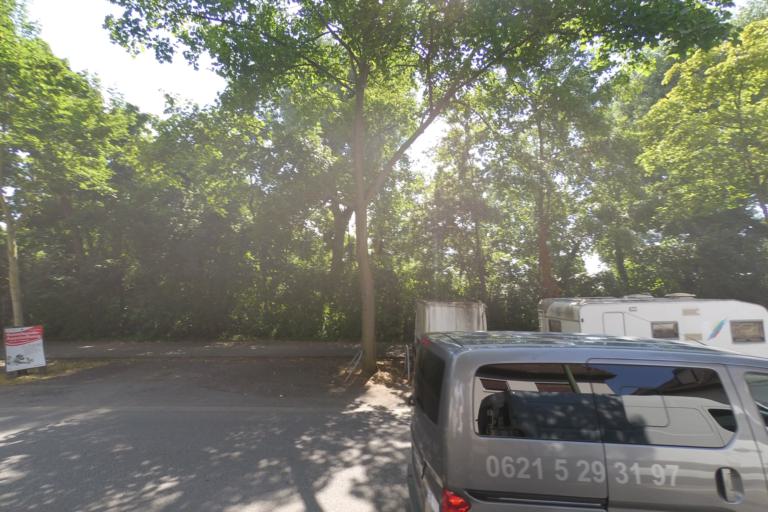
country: DE
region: Rheinland-Pfalz
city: Ludwigshafen am Rhein
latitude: 49.4919
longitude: 8.4144
